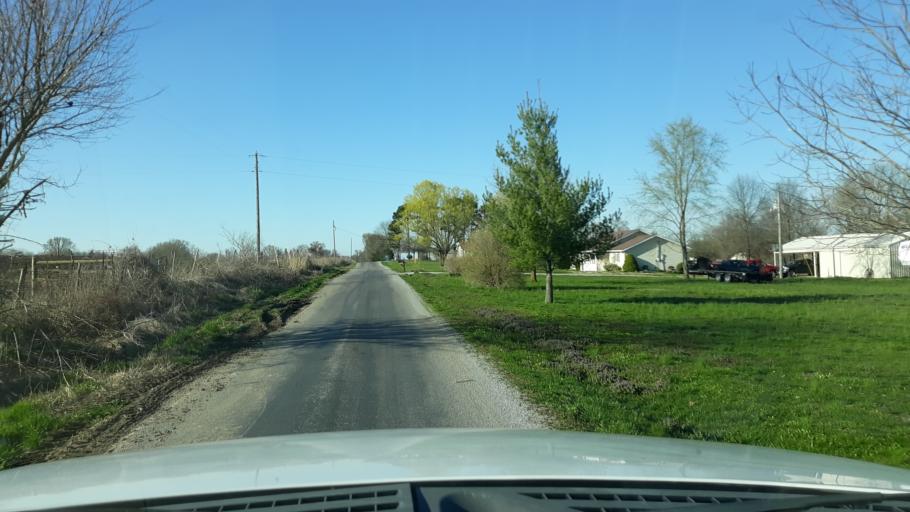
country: US
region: Illinois
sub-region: Saline County
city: Harrisburg
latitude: 37.7806
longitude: -88.6013
